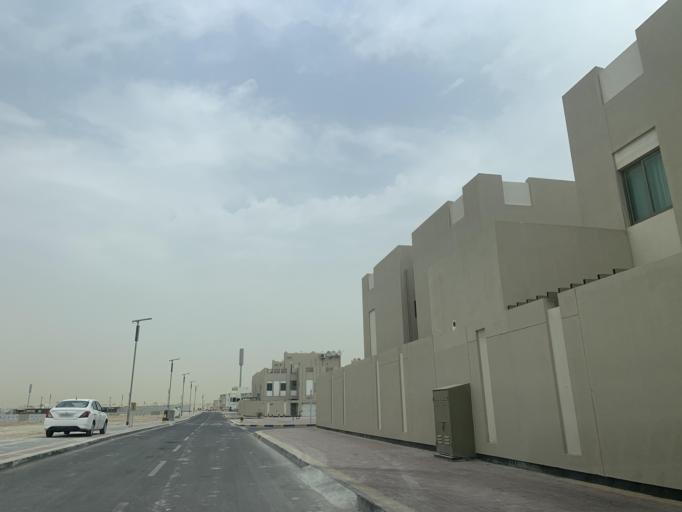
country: BH
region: Northern
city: Madinat `Isa
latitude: 26.1711
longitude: 50.5081
